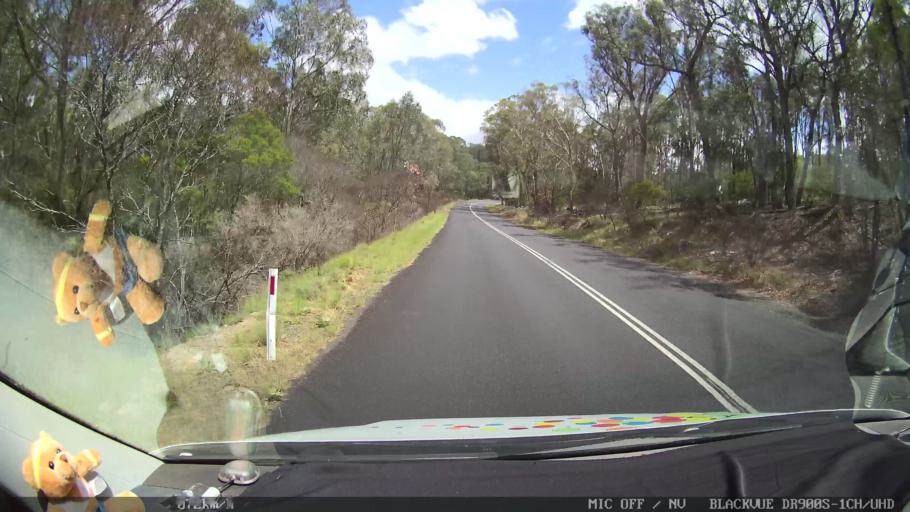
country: AU
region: New South Wales
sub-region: Glen Innes Severn
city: Glen Innes
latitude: -29.5579
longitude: 151.6670
